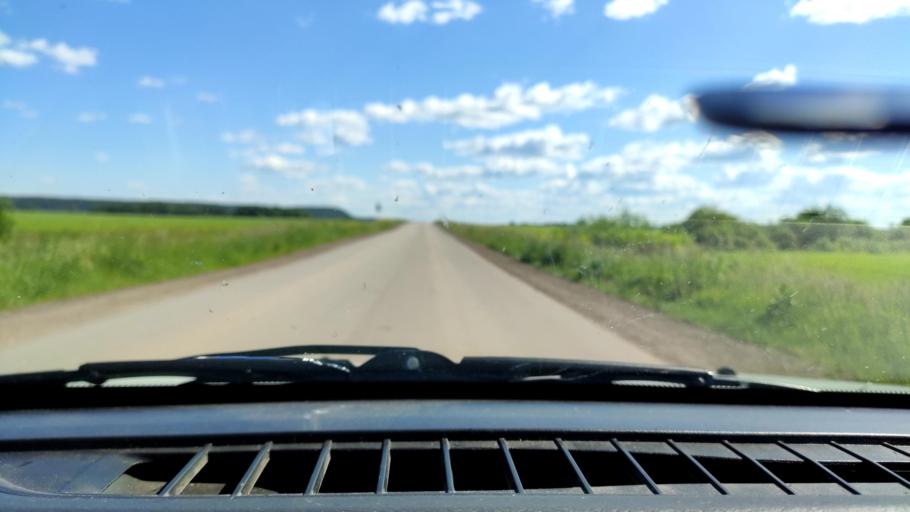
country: RU
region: Perm
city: Orda
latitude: 57.2243
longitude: 56.5732
